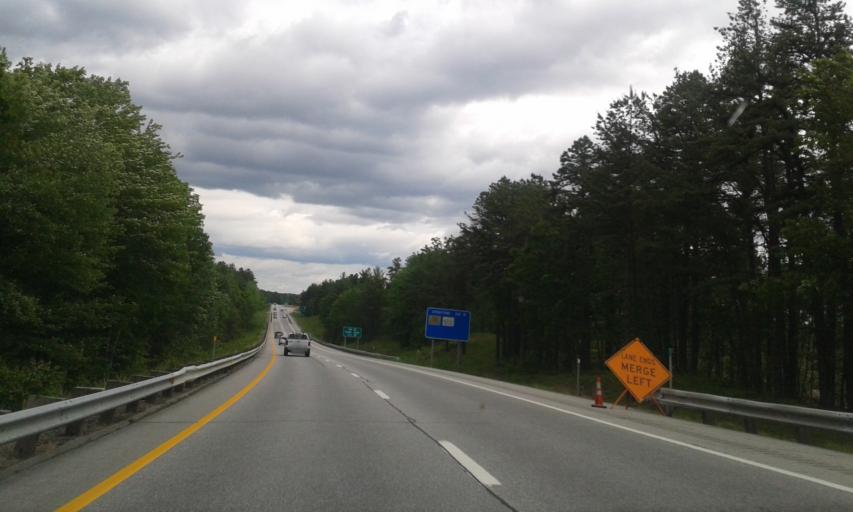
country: US
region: New Hampshire
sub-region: Merrimack County
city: Boscawen
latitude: 43.3376
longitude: -71.6150
